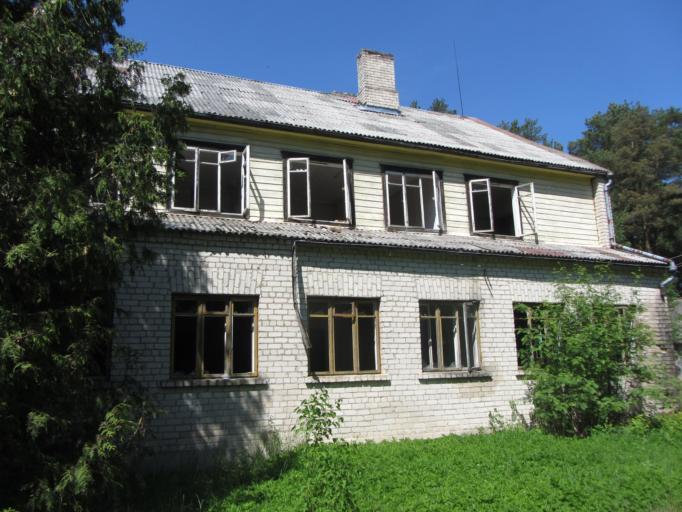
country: LT
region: Utenos apskritis
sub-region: Utena
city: Utena
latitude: 55.6842
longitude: 25.6777
